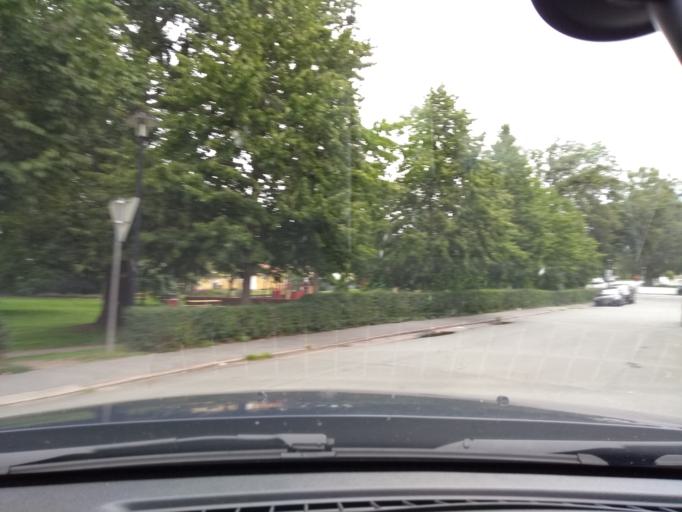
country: SE
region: Joenkoeping
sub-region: Eksjo Kommun
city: Eksjoe
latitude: 57.6685
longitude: 14.9720
